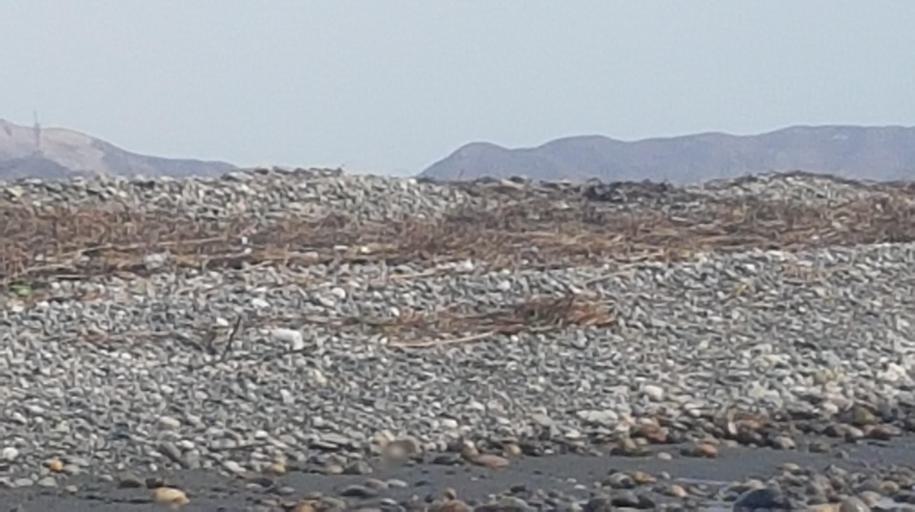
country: PE
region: La Libertad
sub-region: Viru
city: Guadalupito
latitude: -8.9642
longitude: -78.6456
